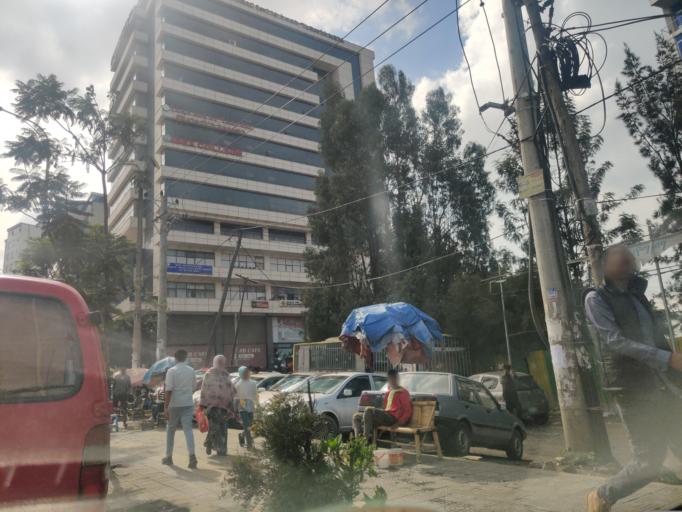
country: ET
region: Adis Abeba
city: Addis Ababa
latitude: 9.0161
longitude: 38.7899
